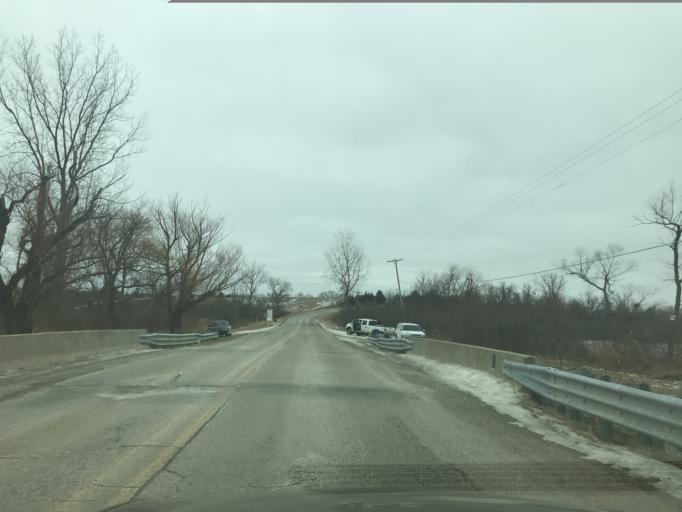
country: US
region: Michigan
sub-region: Jackson County
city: Brooklyn
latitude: 42.0611
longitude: -84.3254
